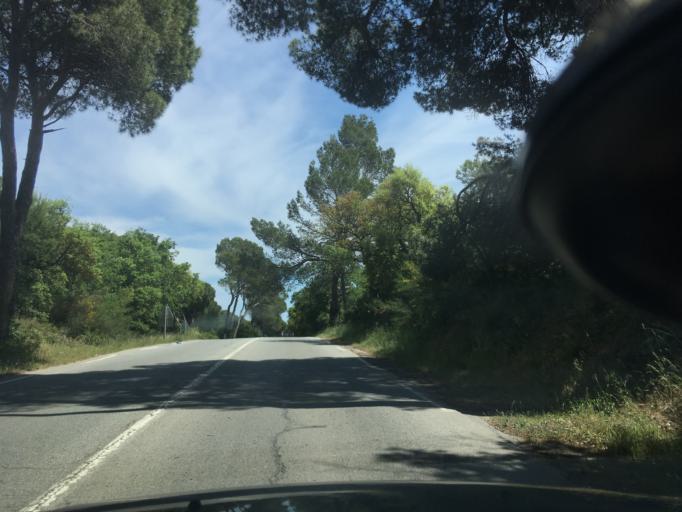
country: FR
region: Provence-Alpes-Cote d'Azur
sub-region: Departement du Var
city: Puget-sur-Argens
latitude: 43.4609
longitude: 6.6609
